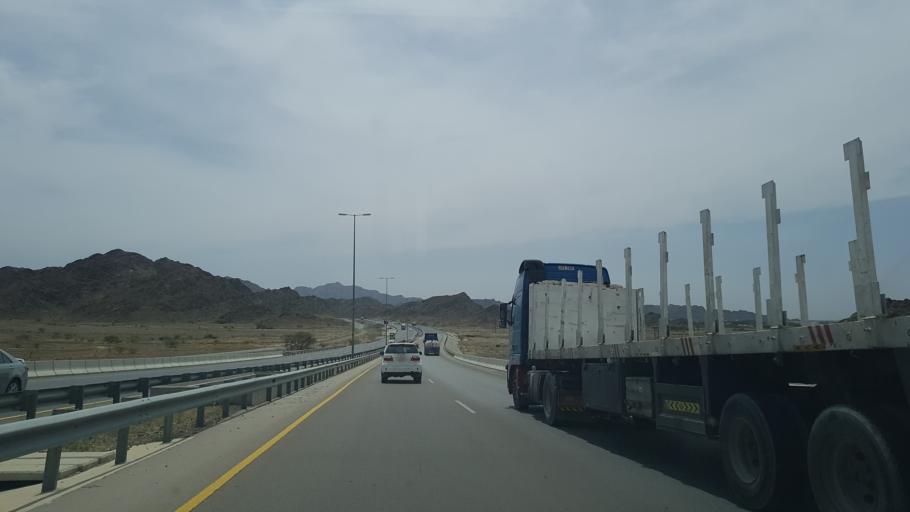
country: OM
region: Muhafazat ad Dakhiliyah
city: Izki
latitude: 22.9593
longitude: 57.7865
